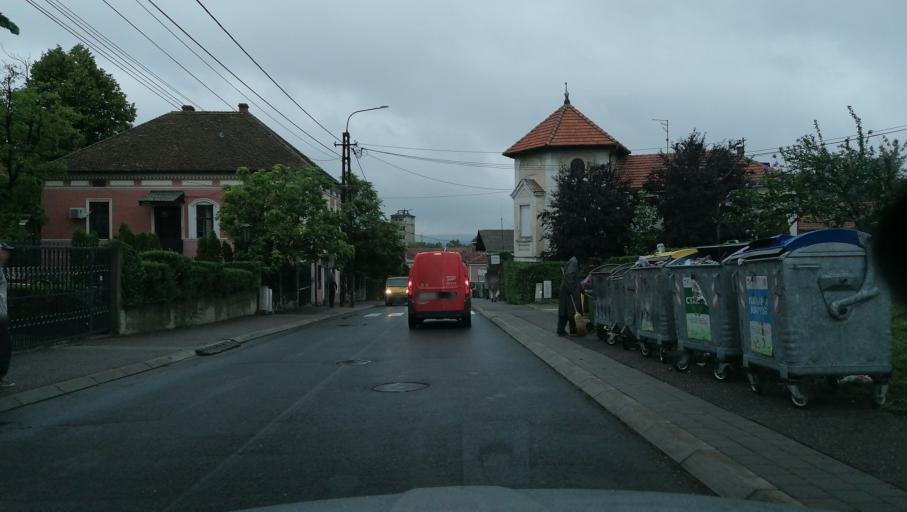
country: RS
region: Central Serbia
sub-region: Rasinski Okrug
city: Krusevac
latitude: 43.5834
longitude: 21.3200
